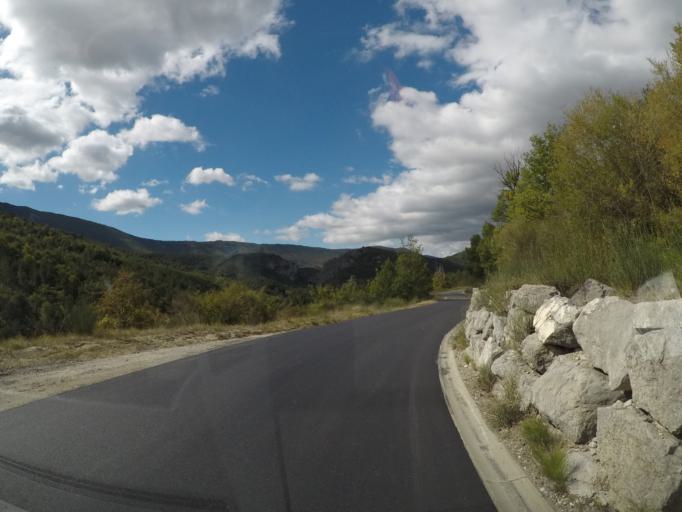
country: FR
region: Provence-Alpes-Cote d'Azur
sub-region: Departement des Hautes-Alpes
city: Laragne-Monteglin
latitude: 44.1758
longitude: 5.6539
